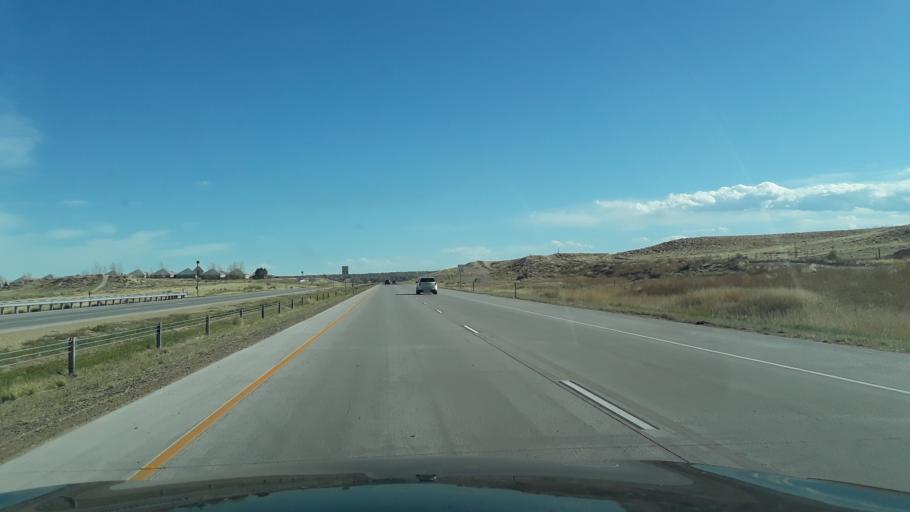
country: US
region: Colorado
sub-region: Pueblo County
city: Pueblo
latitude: 38.2915
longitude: -104.6637
